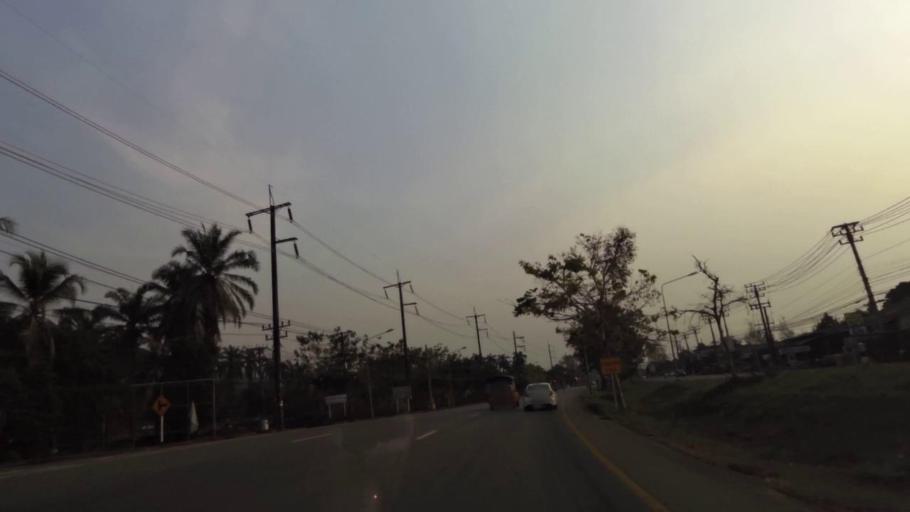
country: TH
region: Chanthaburi
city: Khlung
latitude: 12.5125
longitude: 102.1690
